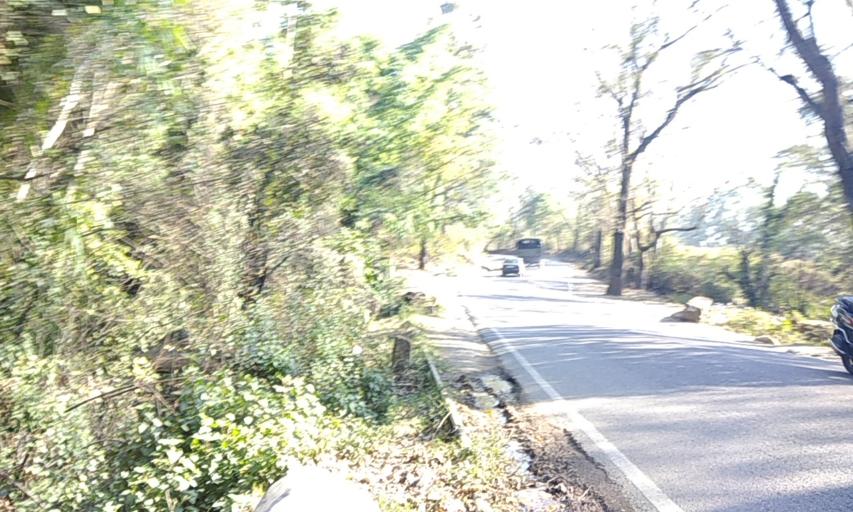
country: IN
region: Himachal Pradesh
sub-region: Kangra
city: Palampur
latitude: 32.1041
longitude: 76.5546
